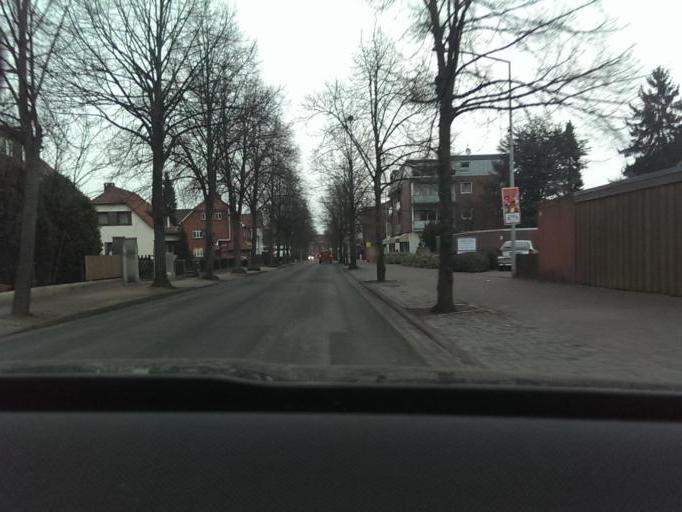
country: DE
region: Lower Saxony
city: Isernhagen Farster Bauerschaft
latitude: 52.4881
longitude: 9.8595
